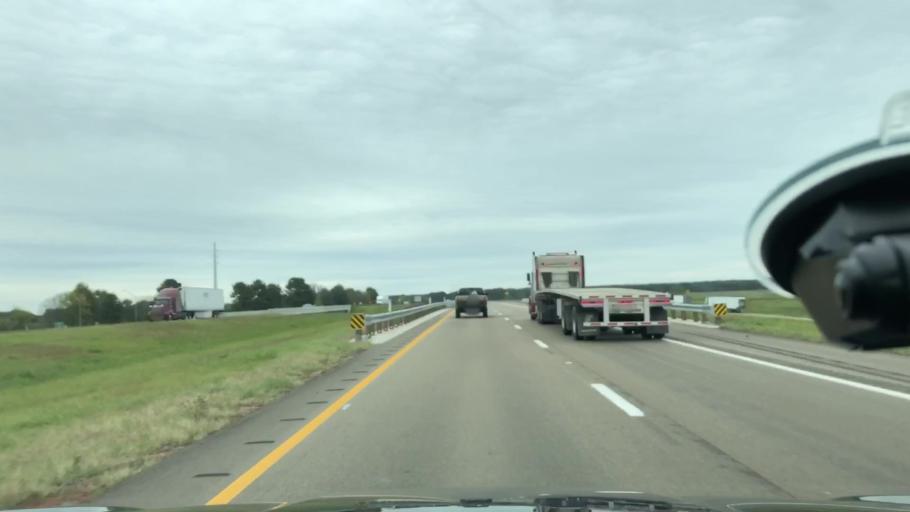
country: US
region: Texas
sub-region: Morris County
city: Naples
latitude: 33.2942
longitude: -94.7387
